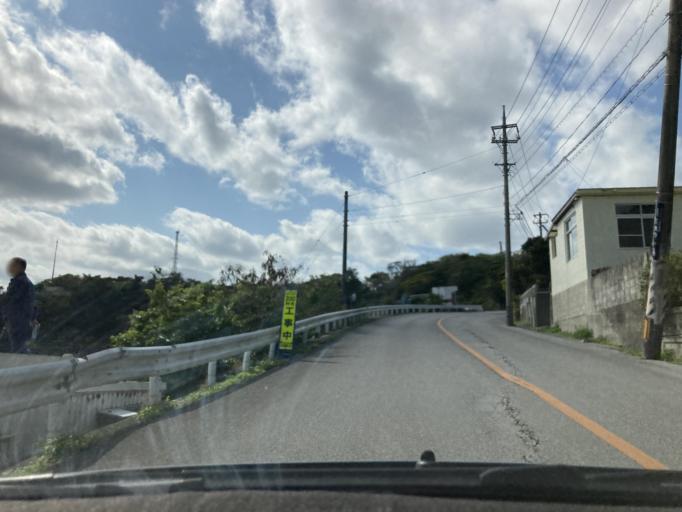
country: JP
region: Okinawa
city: Tomigusuku
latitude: 26.1832
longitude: 127.7602
